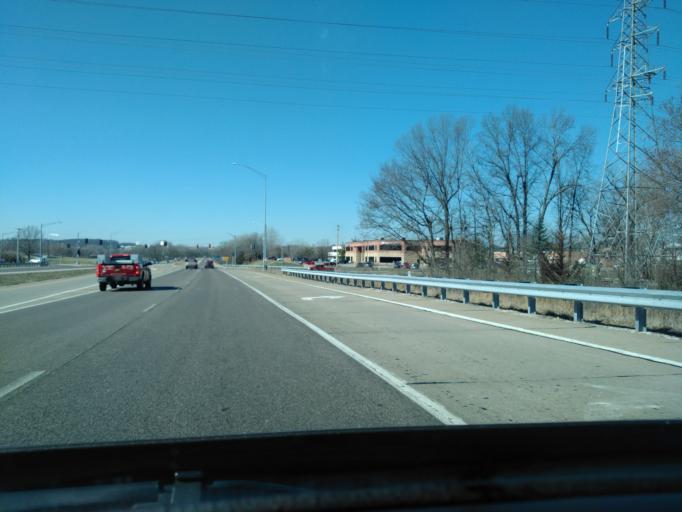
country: US
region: Missouri
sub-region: Saint Louis County
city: Sunset Hills
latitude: 38.5216
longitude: -90.4151
